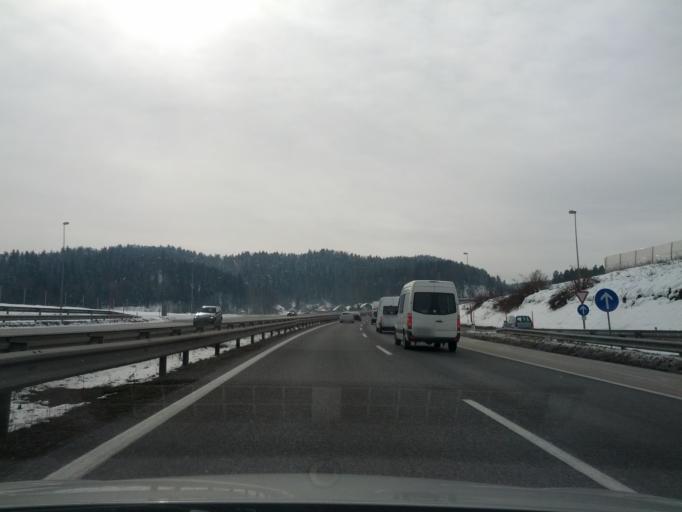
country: SI
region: Skofljica
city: Lavrica
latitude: 46.0422
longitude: 14.5765
